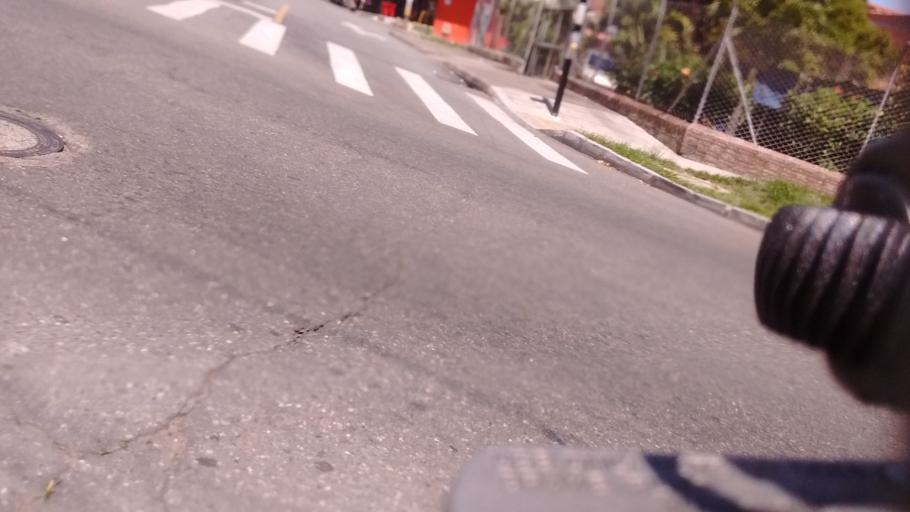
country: CO
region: Antioquia
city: Medellin
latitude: 6.2824
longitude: -75.5818
